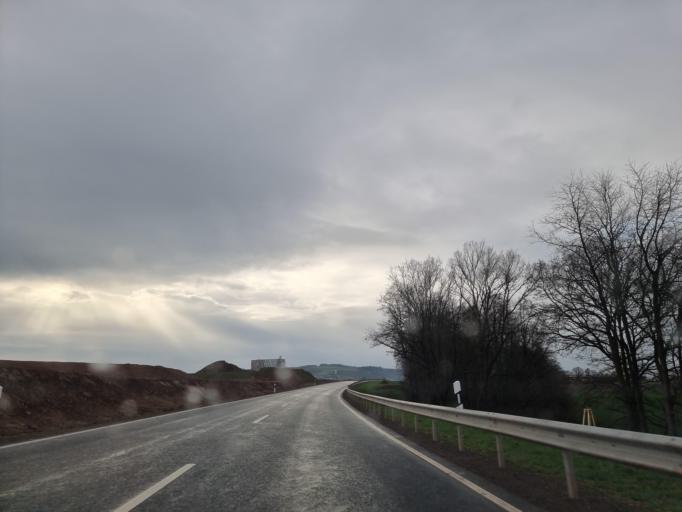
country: DE
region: Rheinland-Pfalz
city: Hetzerath
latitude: 49.8693
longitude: 6.8043
